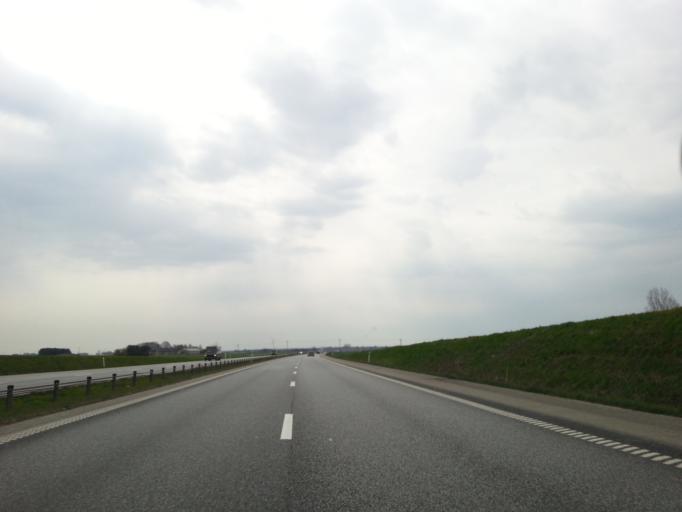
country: SE
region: Skane
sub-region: Landskrona
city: Landskrona
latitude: 55.9096
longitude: 12.8583
